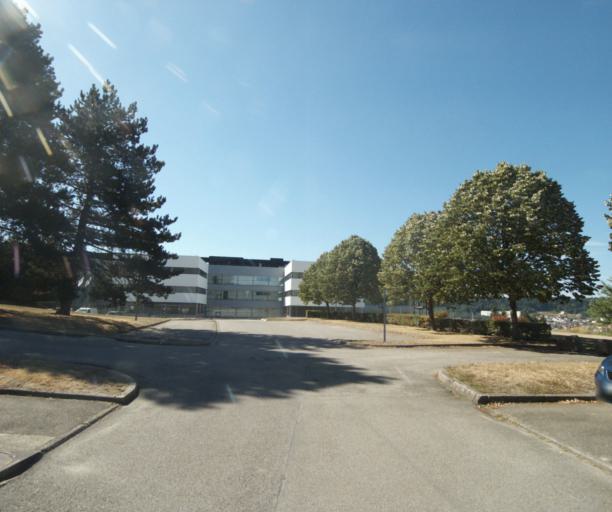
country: FR
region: Lorraine
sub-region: Departement des Vosges
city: Epinal
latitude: 48.1807
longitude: 6.4520
